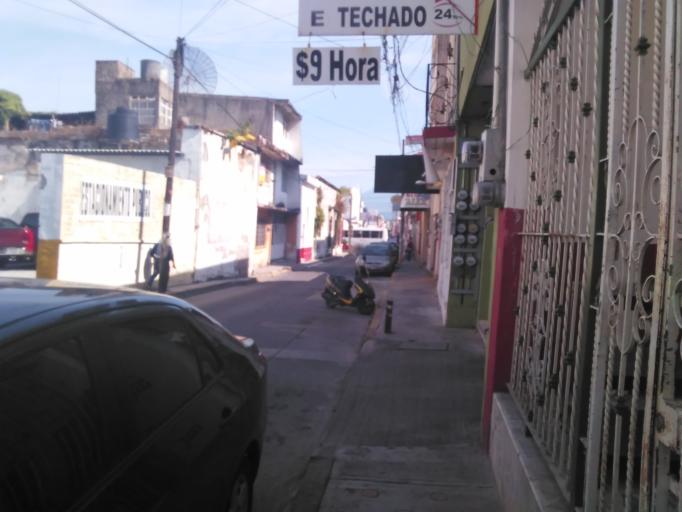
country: MX
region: Nayarit
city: Tepic
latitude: 21.5124
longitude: -104.8959
